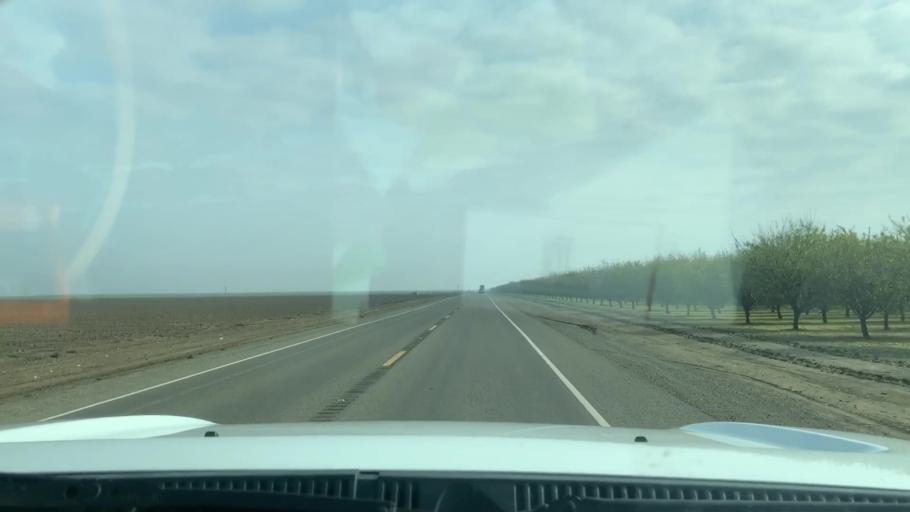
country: US
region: California
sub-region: Fresno County
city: Huron
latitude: 36.2545
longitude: -120.0431
